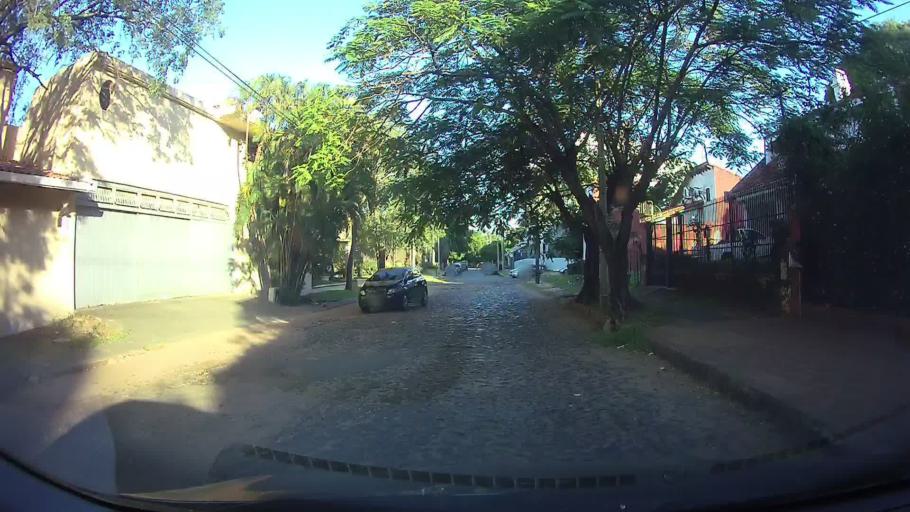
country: PY
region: Asuncion
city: Asuncion
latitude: -25.2807
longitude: -57.5803
